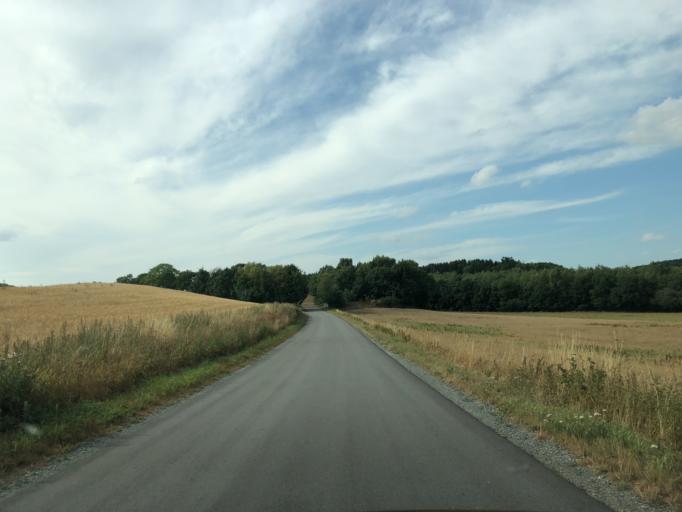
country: DK
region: South Denmark
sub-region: Vejle Kommune
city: Egtved
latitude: 55.6831
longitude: 9.2648
